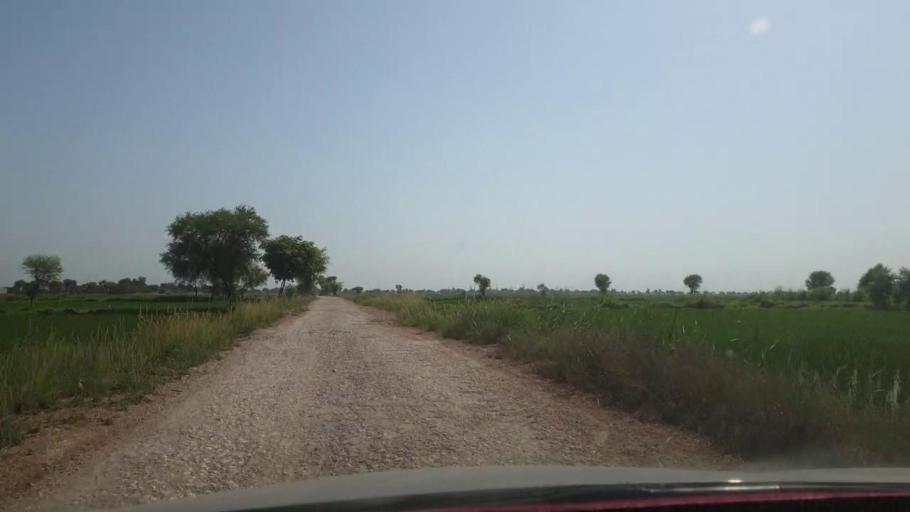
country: PK
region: Sindh
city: Nasirabad
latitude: 27.3635
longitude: 67.8518
